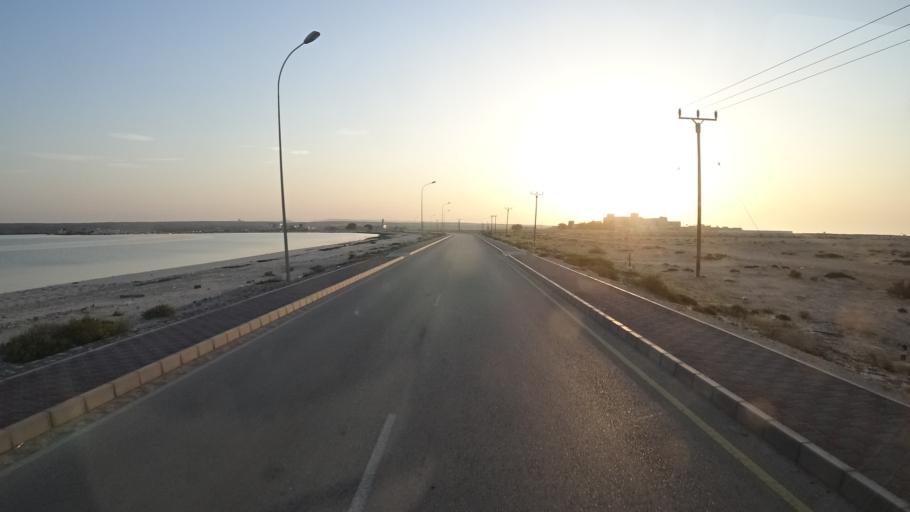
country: OM
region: Ash Sharqiyah
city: Sur
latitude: 22.5289
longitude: 59.7703
